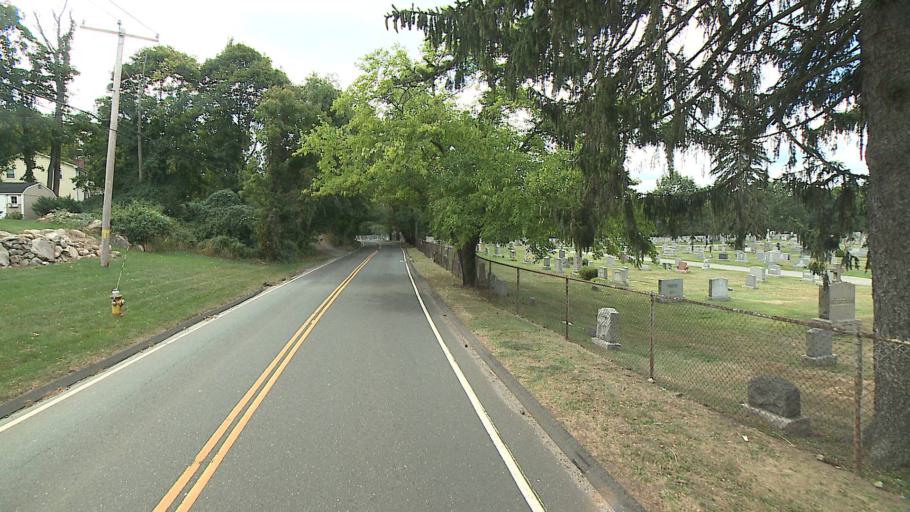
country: US
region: Connecticut
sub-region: Fairfield County
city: Darien
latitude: 41.0909
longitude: -73.5118
